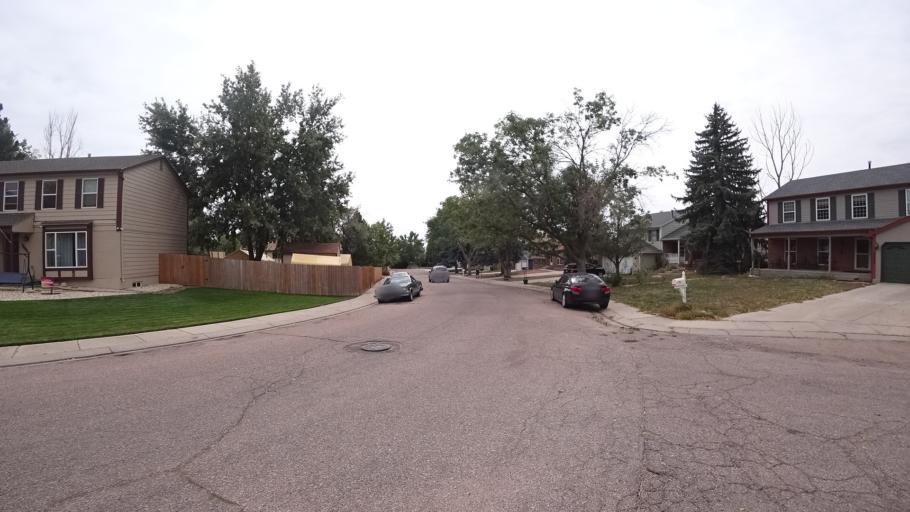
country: US
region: Colorado
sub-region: El Paso County
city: Cimarron Hills
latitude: 38.9034
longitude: -104.7379
